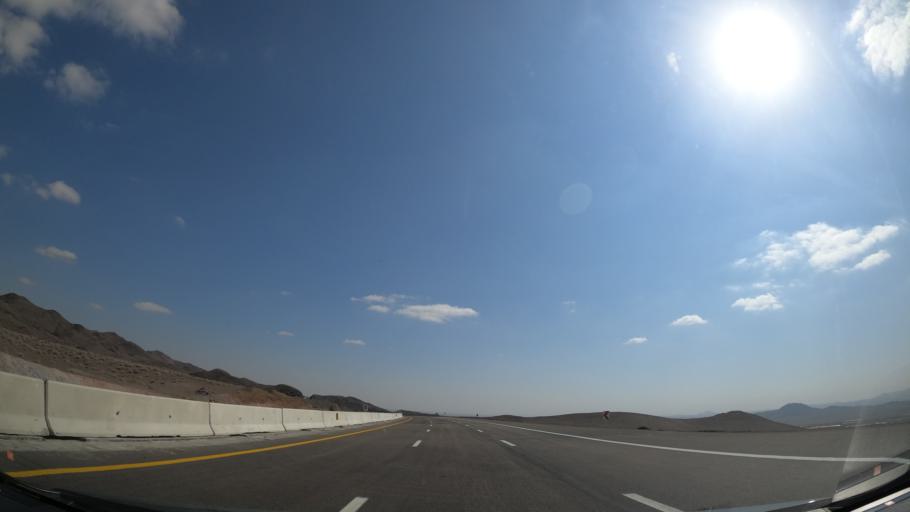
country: IR
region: Alborz
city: Eshtehard
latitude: 35.6659
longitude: 50.6479
